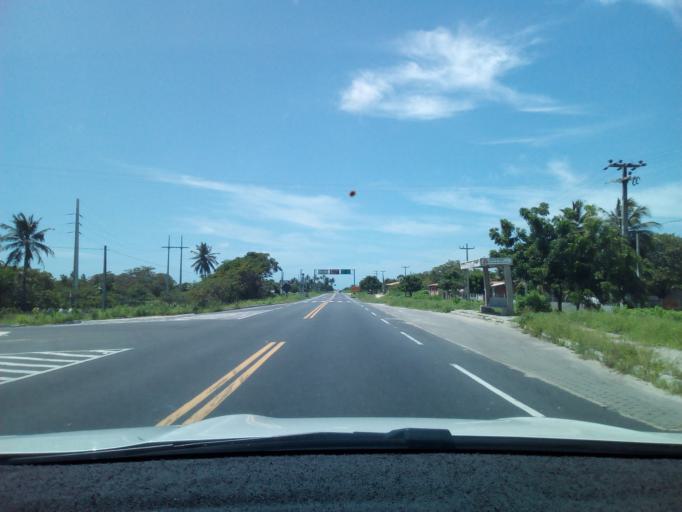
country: BR
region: Ceara
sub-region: Aracati
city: Aracati
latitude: -4.3746
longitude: -37.9258
